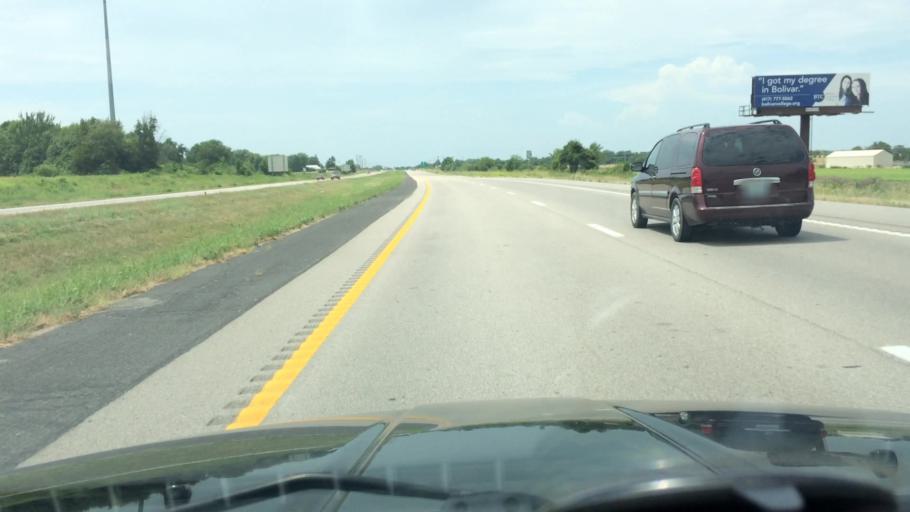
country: US
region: Missouri
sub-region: Polk County
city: Bolivar
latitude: 37.5789
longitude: -93.4035
